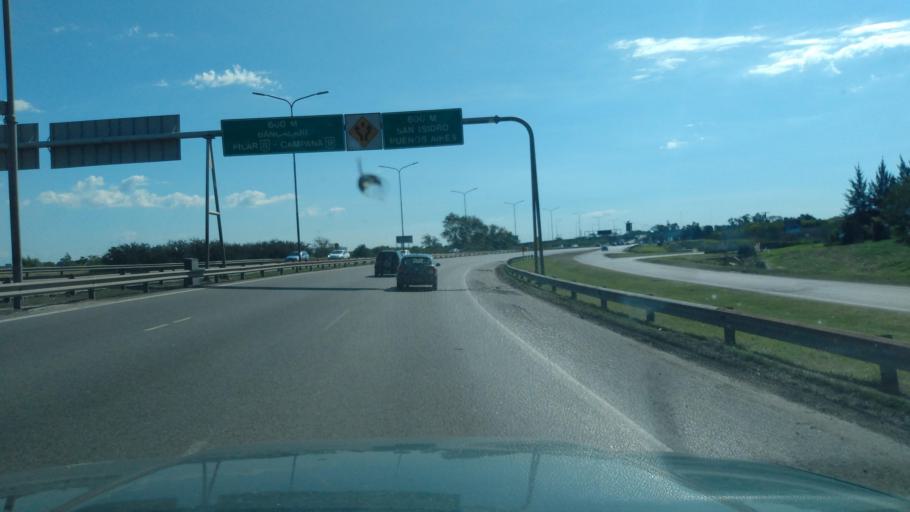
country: AR
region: Buenos Aires
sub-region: Partido de Tigre
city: Tigre
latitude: -34.4954
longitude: -58.5945
